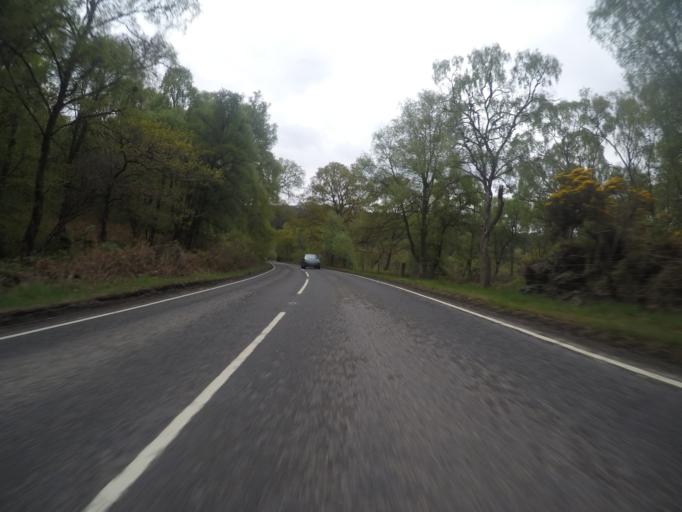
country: GB
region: Scotland
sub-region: Highland
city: Spean Bridge
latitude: 57.1499
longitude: -4.6772
